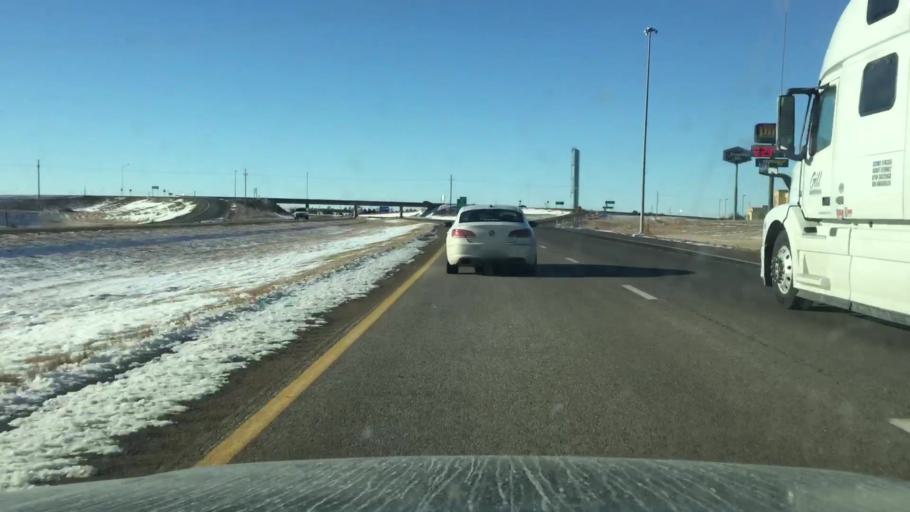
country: US
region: Kansas
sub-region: Thomas County
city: Colby
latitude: 39.3625
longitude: -101.0326
